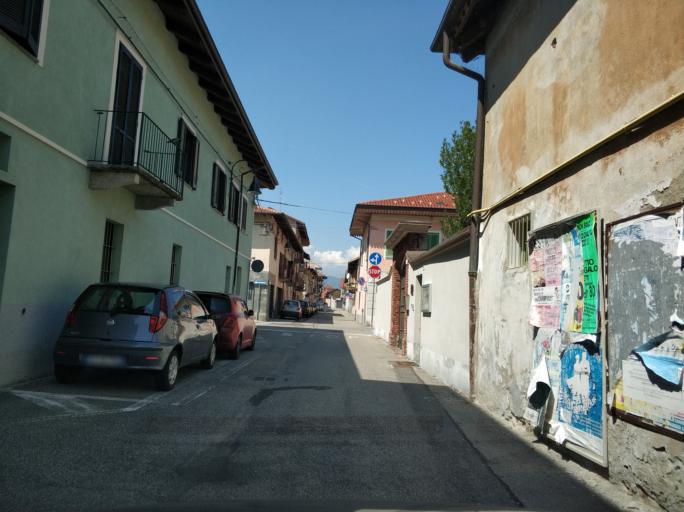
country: IT
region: Piedmont
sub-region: Provincia di Torino
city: San Maurizio
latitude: 45.2178
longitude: 7.6316
